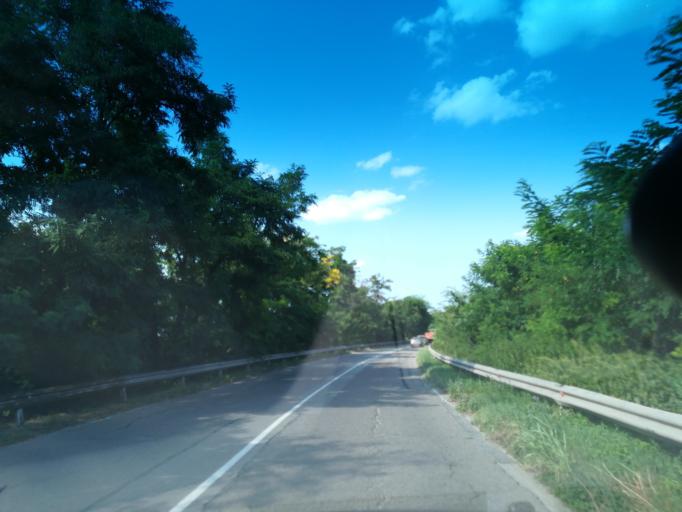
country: BG
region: Stara Zagora
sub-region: Obshtina Chirpan
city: Chirpan
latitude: 42.2367
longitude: 25.3979
